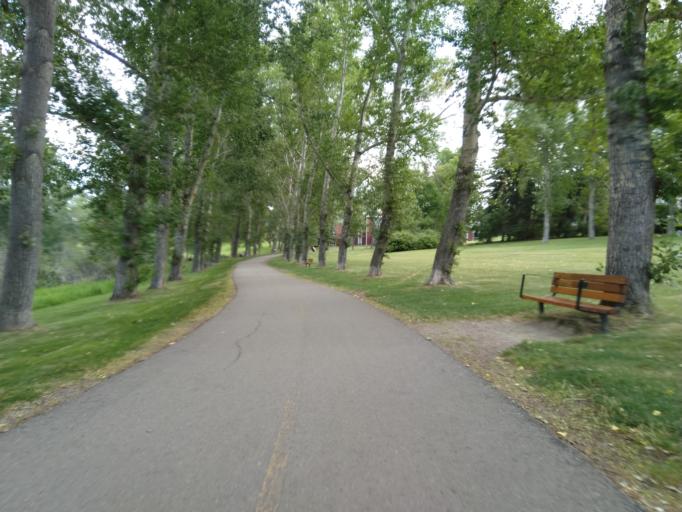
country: CA
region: Alberta
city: Calgary
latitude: 51.0729
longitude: -114.0917
